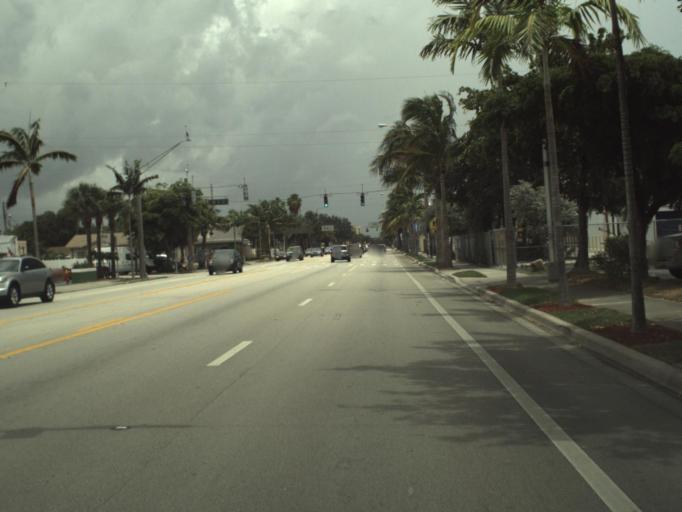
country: US
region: Florida
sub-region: Broward County
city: Dania Beach
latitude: 26.0460
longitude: -80.1434
